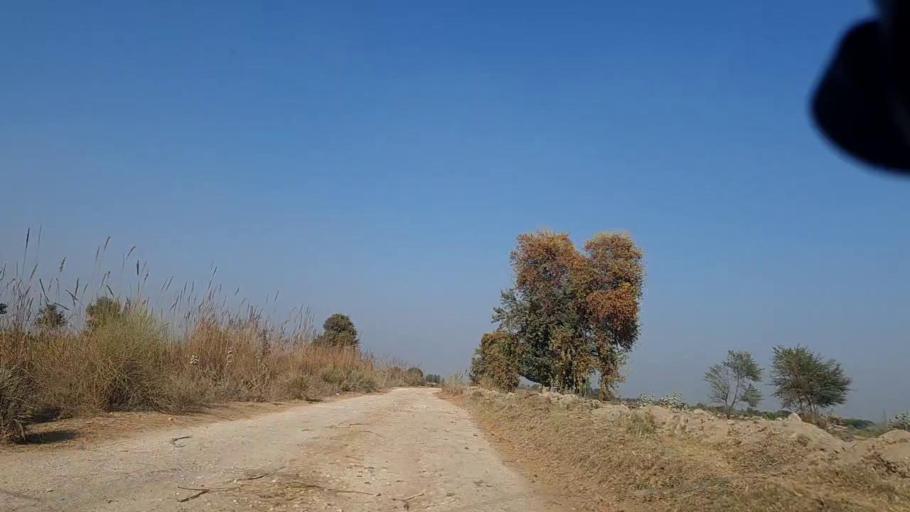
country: PK
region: Sindh
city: Khanpur
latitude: 27.6911
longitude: 69.4973
